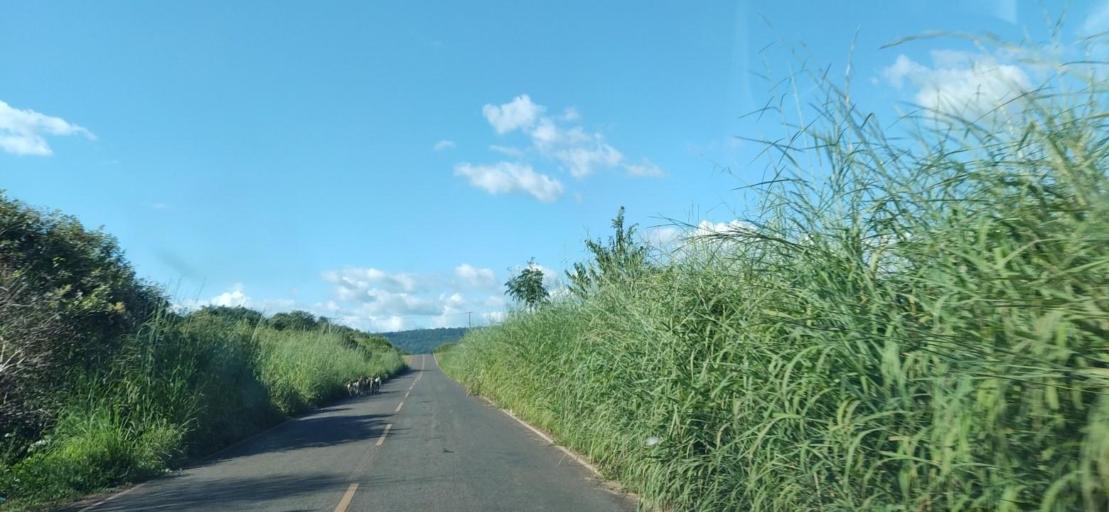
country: BR
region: Piaui
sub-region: Valenca Do Piaui
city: Valenca do Piaui
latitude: -6.1801
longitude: -41.8204
